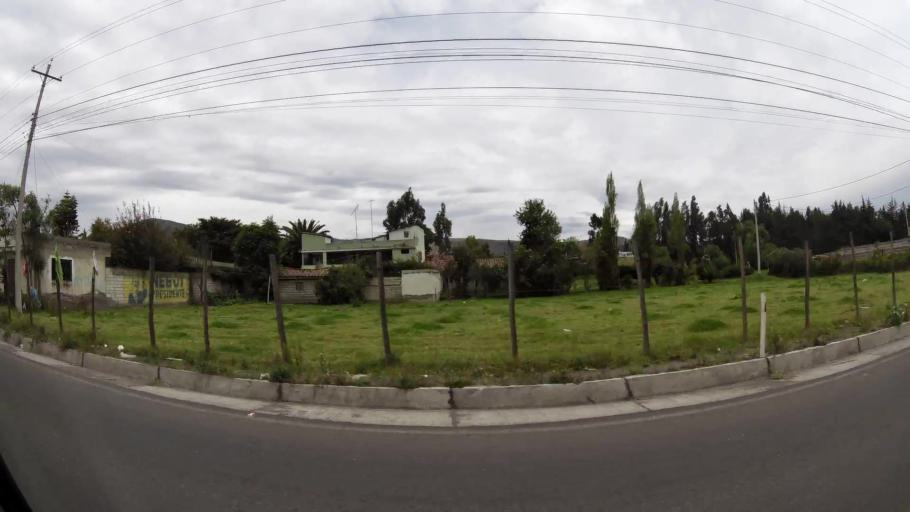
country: EC
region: Cotopaxi
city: San Miguel de Salcedo
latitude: -1.0069
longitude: -78.5934
